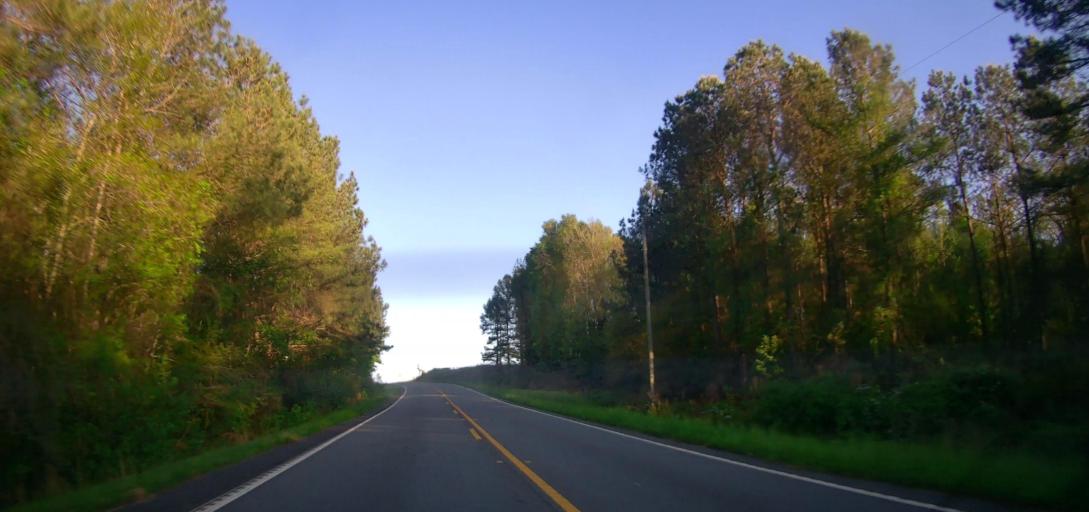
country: US
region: Georgia
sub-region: Schley County
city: Ellaville
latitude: 32.3470
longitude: -84.3734
